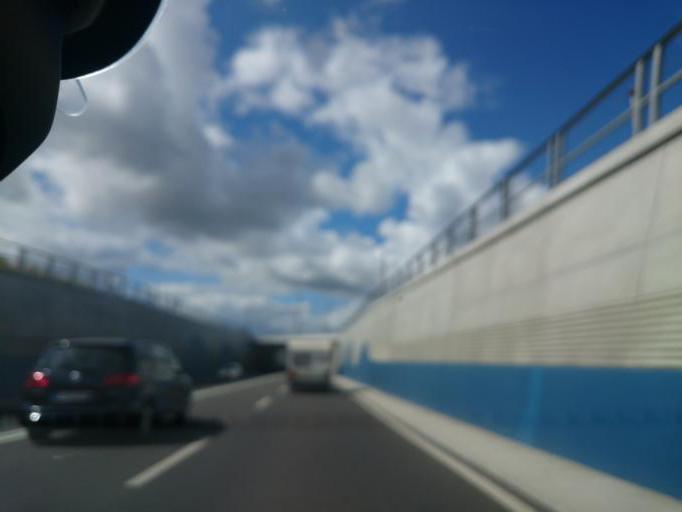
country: DE
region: Mecklenburg-Vorpommern
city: Rambin
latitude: 54.3476
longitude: 13.1769
